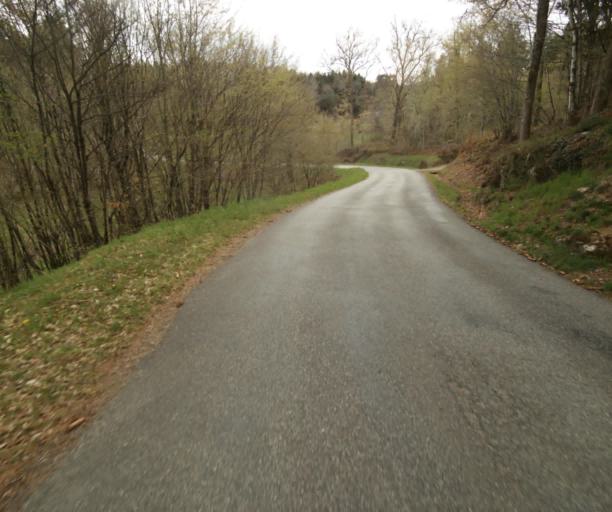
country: FR
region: Limousin
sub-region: Departement de la Correze
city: Argentat
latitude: 45.1954
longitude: 1.9572
